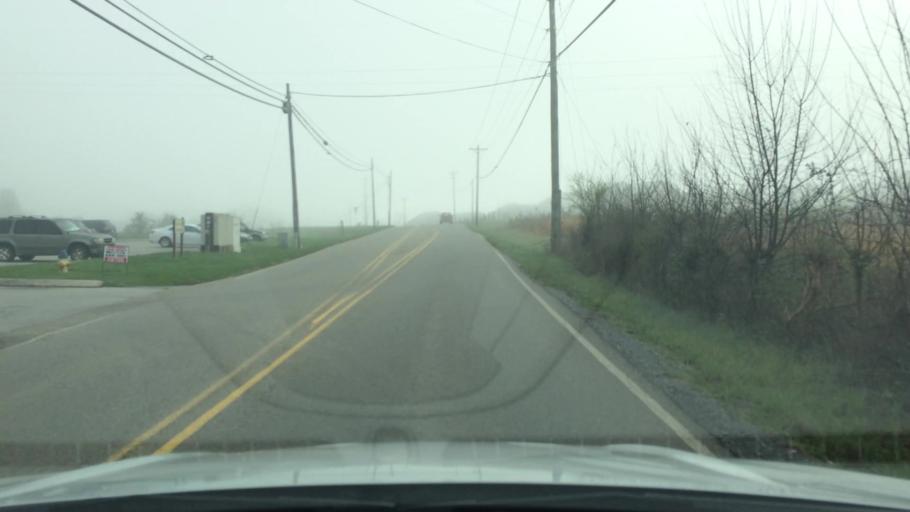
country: US
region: Tennessee
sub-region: Blount County
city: Maryville
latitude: 35.7354
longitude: -84.0208
